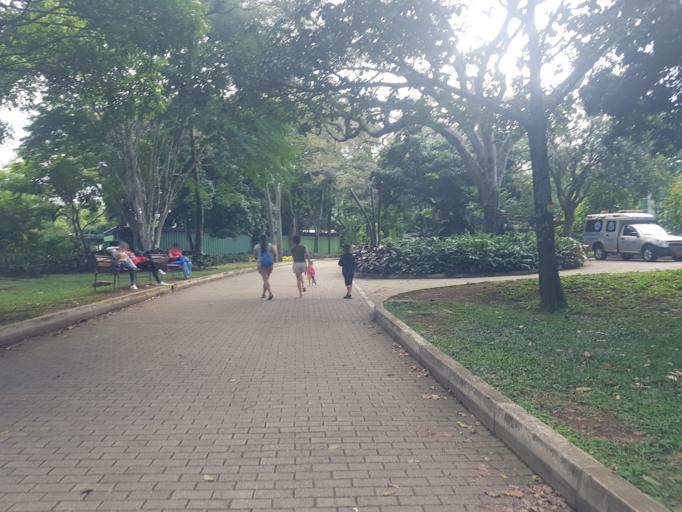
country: CO
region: Antioquia
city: Medellin
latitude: 6.2699
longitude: -75.5623
